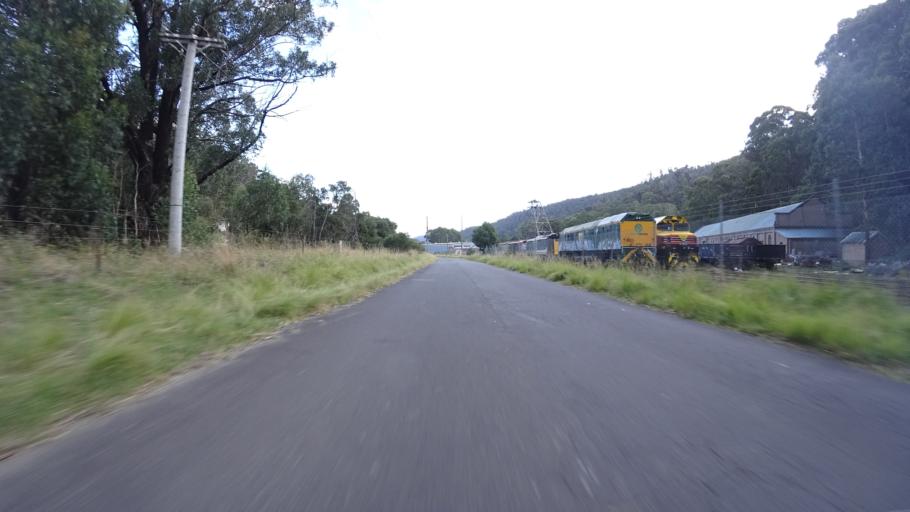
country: AU
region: New South Wales
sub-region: Lithgow
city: Lithgow
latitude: -33.4590
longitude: 150.1703
